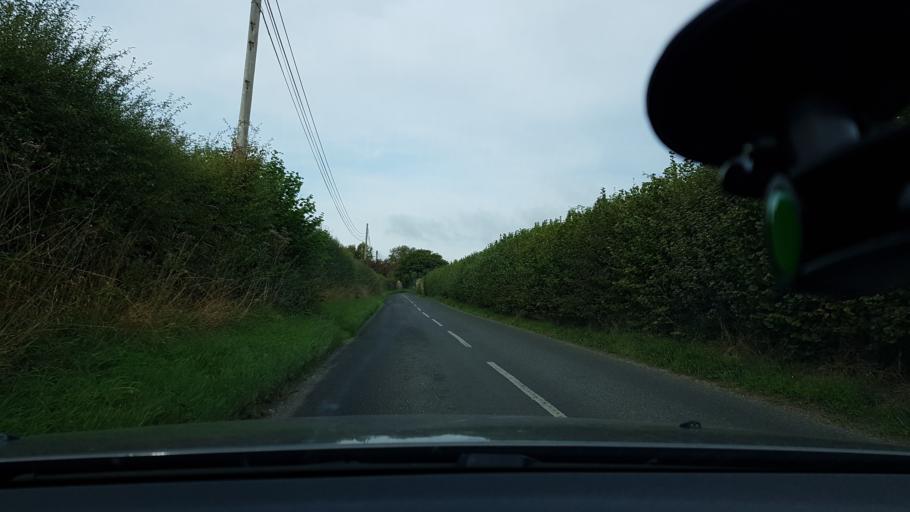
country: GB
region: England
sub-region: West Berkshire
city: Kintbury
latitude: 51.3955
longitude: -1.4365
